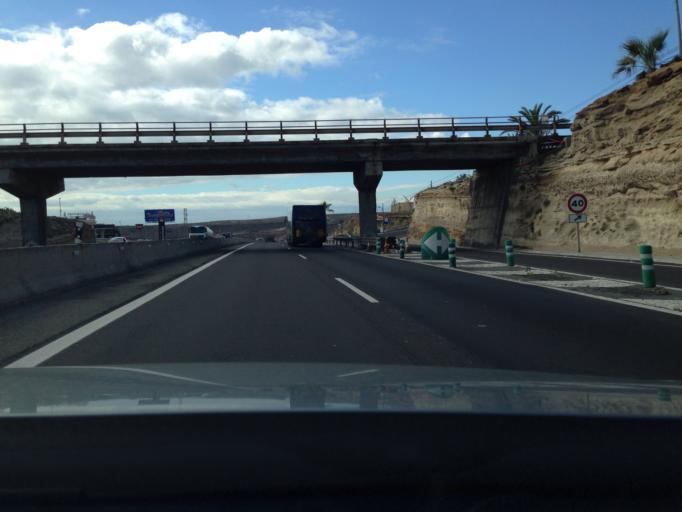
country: ES
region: Canary Islands
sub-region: Provincia de Santa Cruz de Tenerife
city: Lomo de Arico
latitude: 28.1682
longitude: -16.4337
